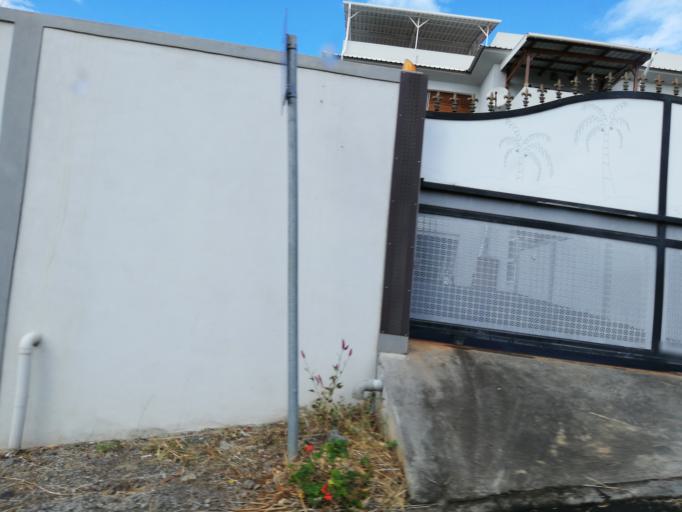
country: MU
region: Black River
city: Petite Riviere
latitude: -20.2032
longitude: 57.4605
